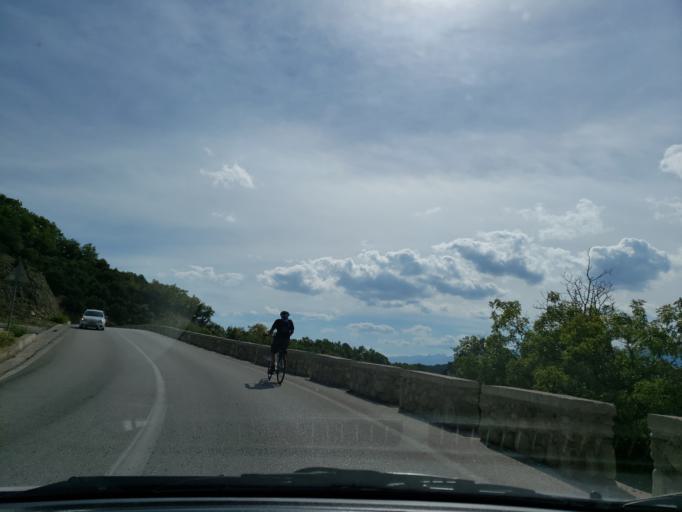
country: GR
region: Thessaly
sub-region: Trikala
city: Kastraki
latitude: 39.7231
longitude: 21.6347
